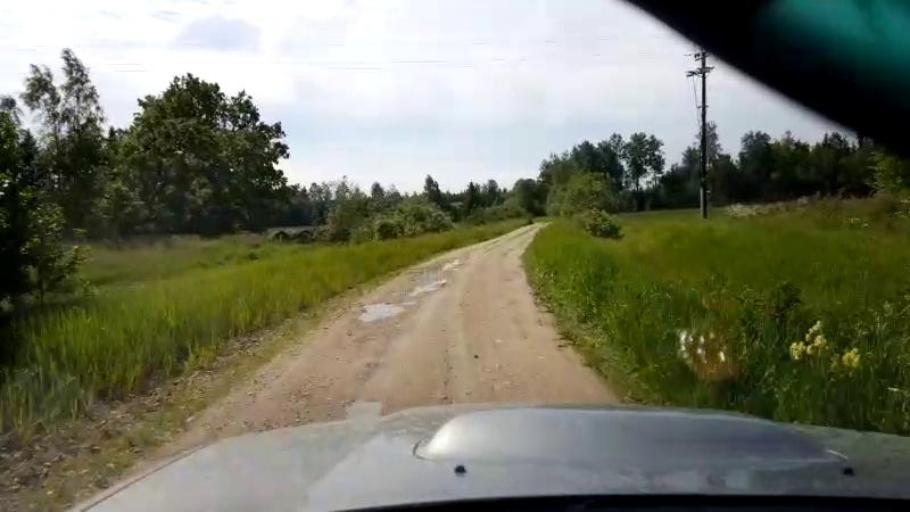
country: EE
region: Paernumaa
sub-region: Sindi linn
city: Sindi
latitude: 58.5277
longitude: 24.6695
